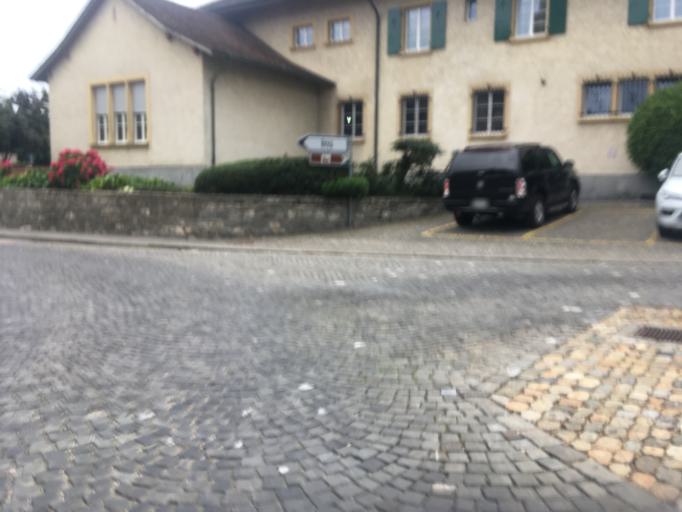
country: CH
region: Bern
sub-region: Seeland District
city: Erlach
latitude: 47.0417
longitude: 7.0962
